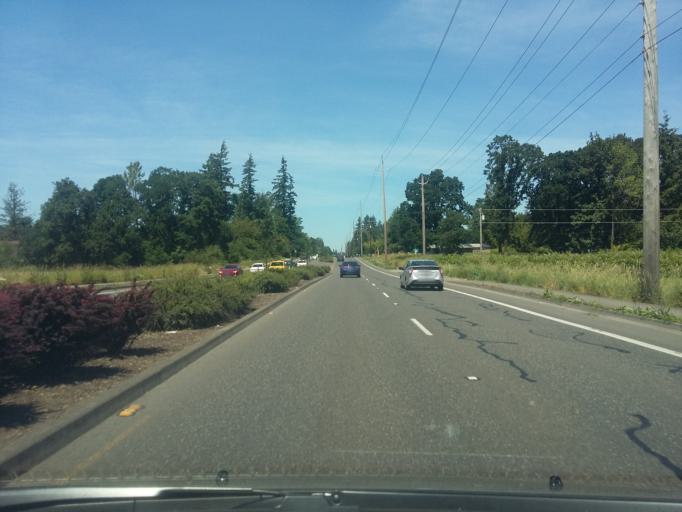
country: US
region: Washington
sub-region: Clark County
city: Mill Plain
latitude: 45.6641
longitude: -122.5059
